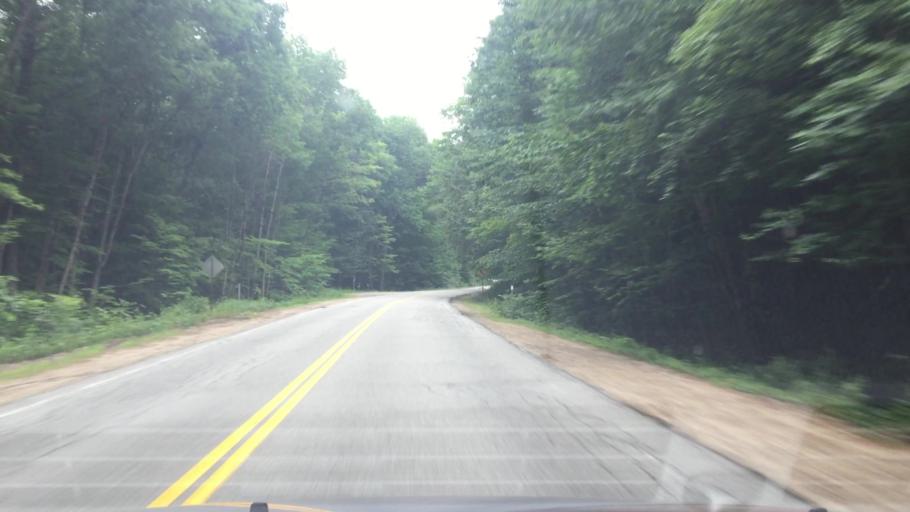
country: US
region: New Hampshire
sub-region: Carroll County
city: North Conway
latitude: 44.0982
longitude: -71.1728
